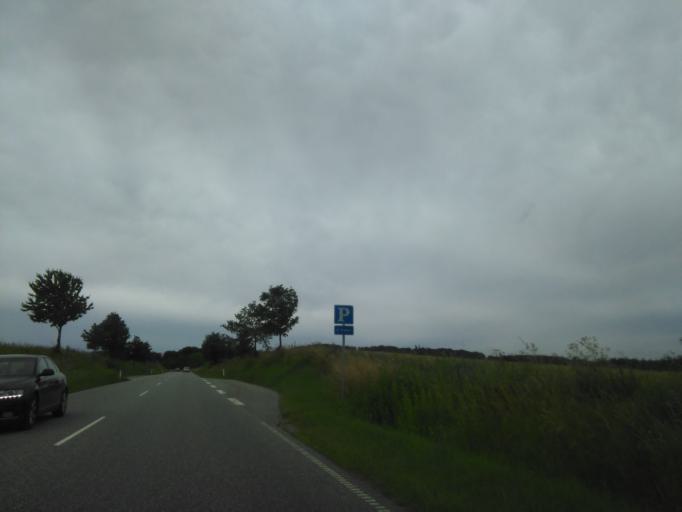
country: DK
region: Central Jutland
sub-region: Skanderborg Kommune
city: Skanderborg
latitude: 55.9580
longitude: 9.9852
